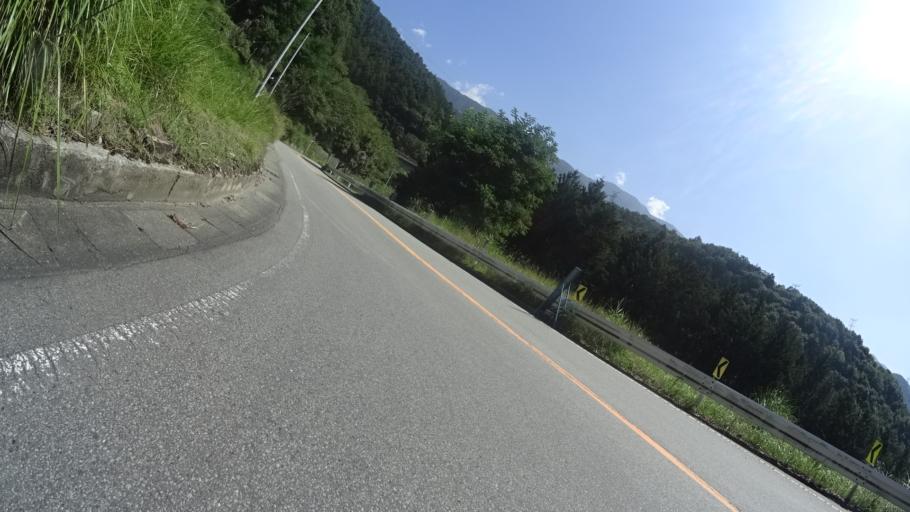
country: JP
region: Yamanashi
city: Enzan
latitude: 35.7400
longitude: 138.8011
